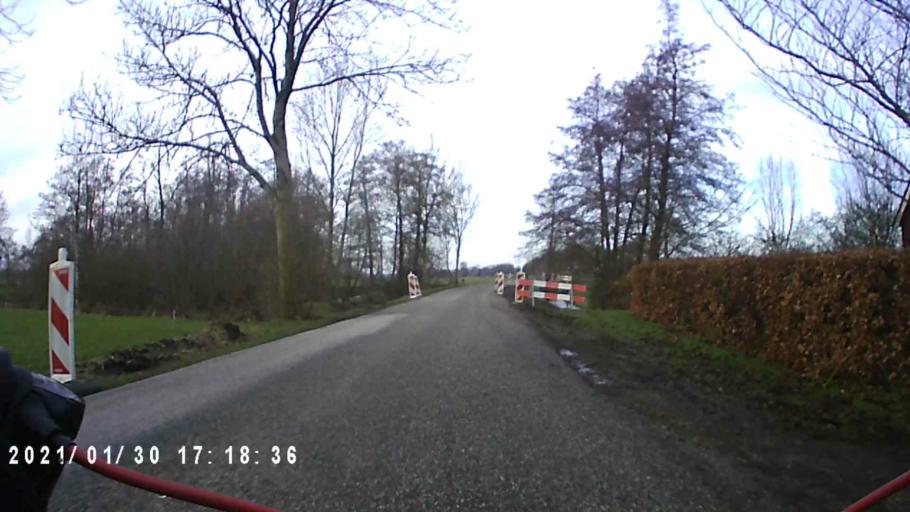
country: NL
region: Groningen
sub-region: Gemeente Leek
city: Leek
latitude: 53.1863
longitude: 6.3570
